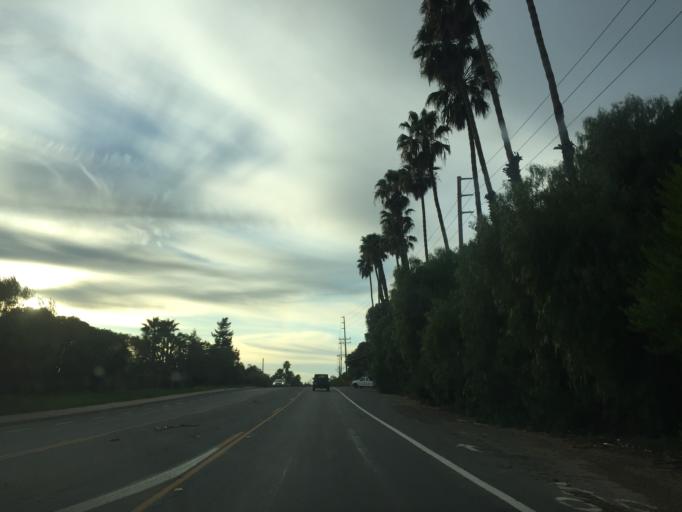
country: US
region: California
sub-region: Santa Barbara County
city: Goleta
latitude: 34.4516
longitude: -119.7925
